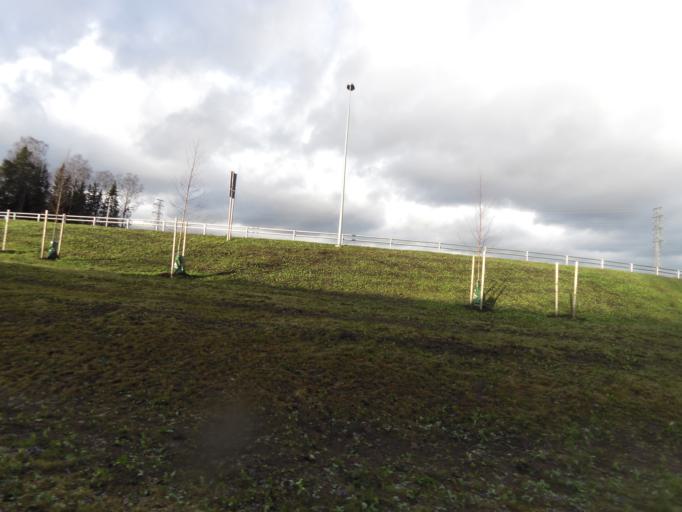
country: FI
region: Uusimaa
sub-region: Helsinki
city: Kilo
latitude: 60.2054
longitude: 24.7870
